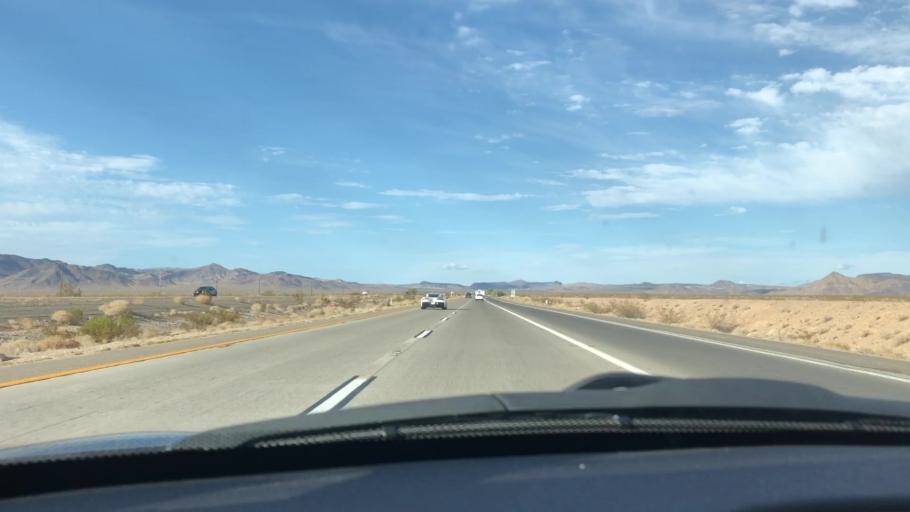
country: US
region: Nevada
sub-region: Clark County
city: Sandy Valley
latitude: 35.3053
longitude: -116.0117
